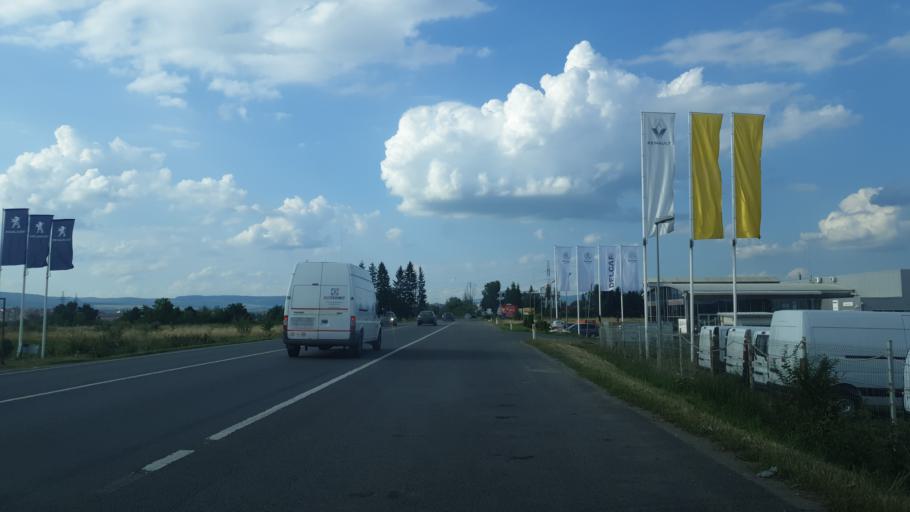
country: RO
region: Covasna
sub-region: Municipiul Sfantu Gheorghe
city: Sfantu-Gheorghe
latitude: 45.8436
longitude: 25.8039
